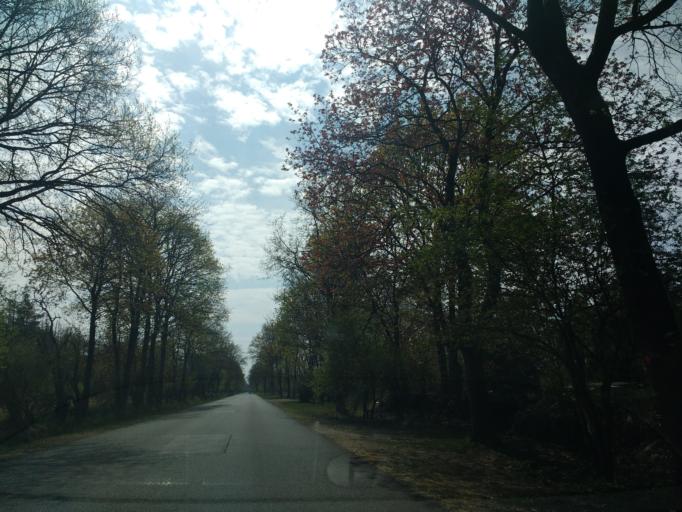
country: DE
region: North Rhine-Westphalia
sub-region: Regierungsbezirk Detmold
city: Hovelhof
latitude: 51.8156
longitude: 8.7224
